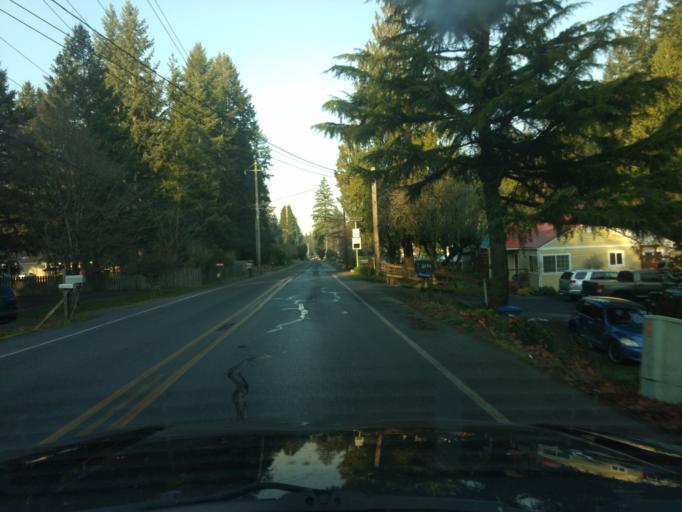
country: US
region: Washington
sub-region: Kitsap County
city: Erlands Point-Kitsap Lake
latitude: 47.5824
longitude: -122.7149
